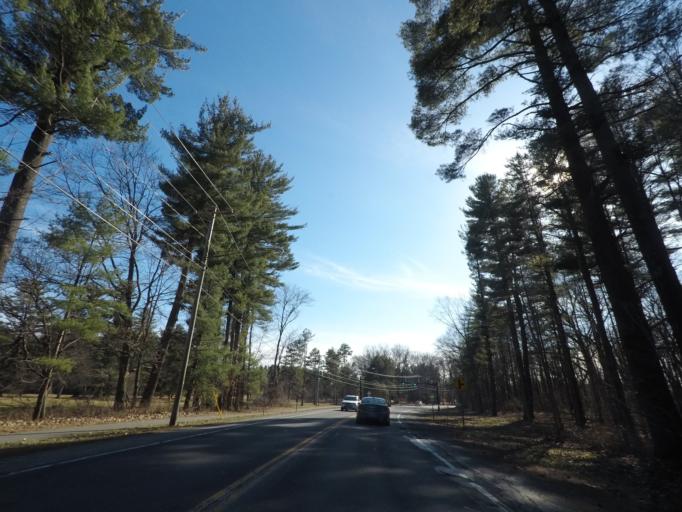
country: US
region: New York
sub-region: Saratoga County
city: Saratoga Springs
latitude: 43.0626
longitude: -73.8001
